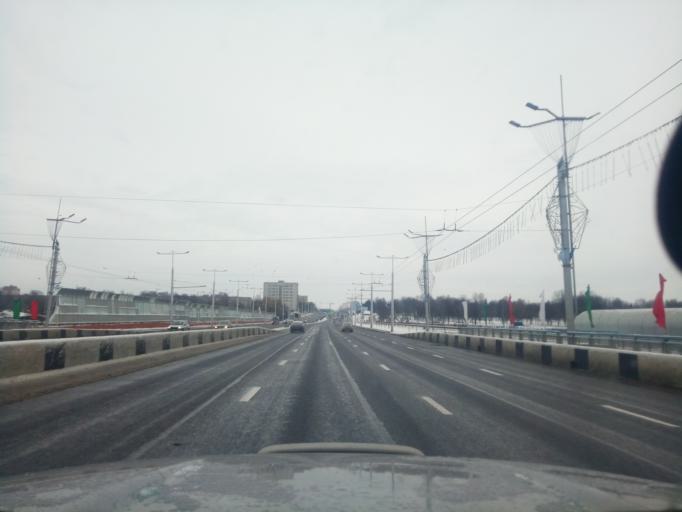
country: BY
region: Minsk
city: Hatava
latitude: 53.8532
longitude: 27.6340
